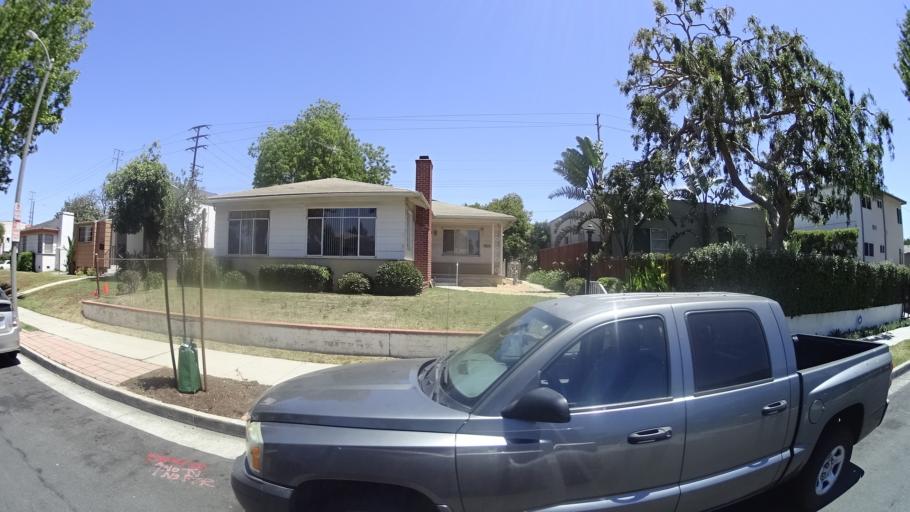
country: US
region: California
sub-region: Los Angeles County
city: Santa Monica
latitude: 34.0208
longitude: -118.4727
